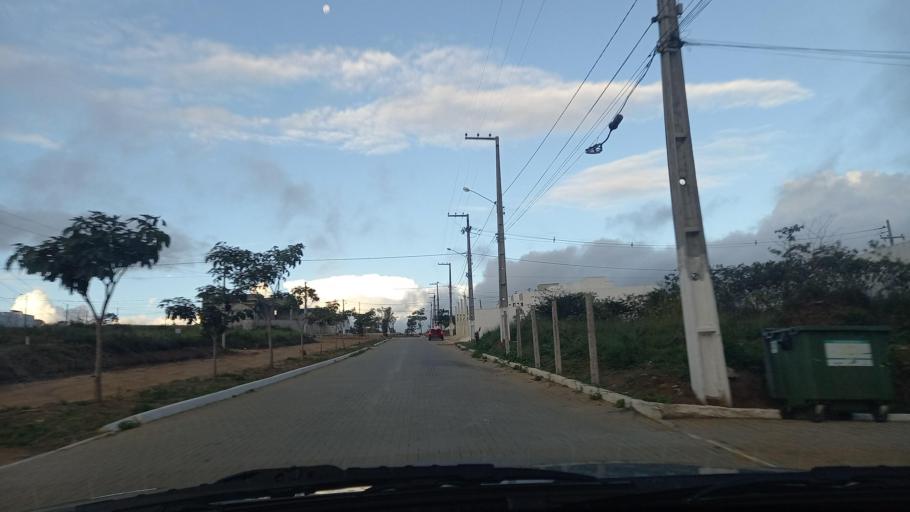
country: BR
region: Pernambuco
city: Garanhuns
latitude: -8.8923
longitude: -36.4397
